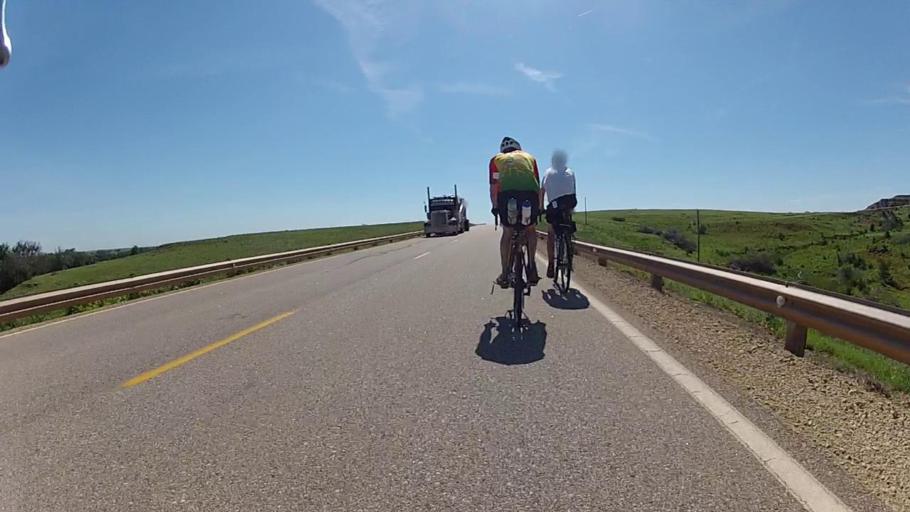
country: US
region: Kansas
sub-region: Barber County
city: Medicine Lodge
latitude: 37.2752
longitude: -98.7102
